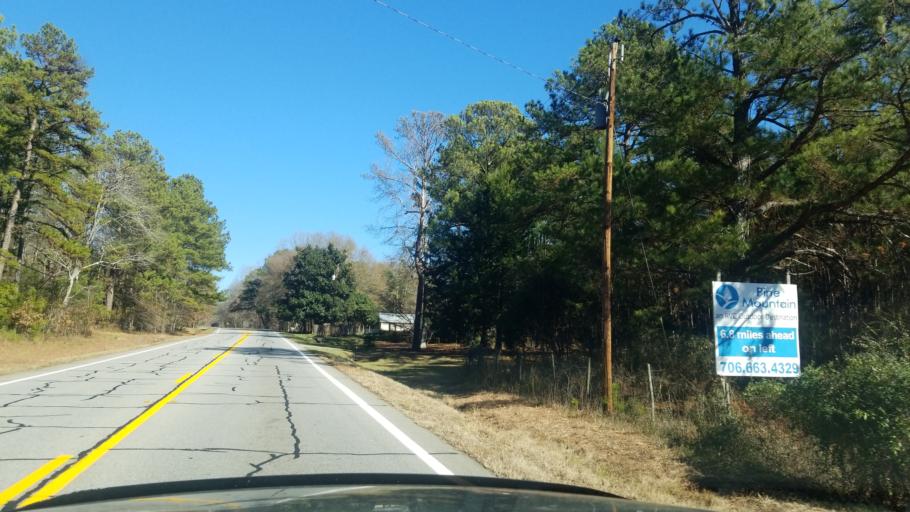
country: US
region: Georgia
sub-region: Harris County
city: Hamilton
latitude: 32.8008
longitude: -84.8649
